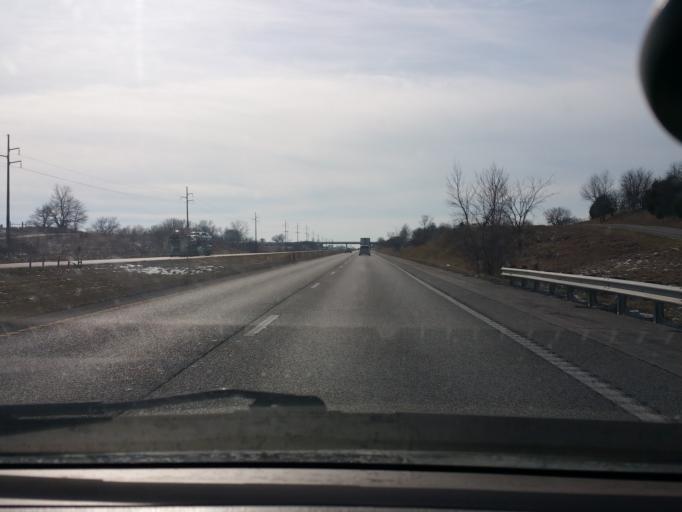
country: US
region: Missouri
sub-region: Clay County
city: Kearney
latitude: 39.3295
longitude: -94.3931
